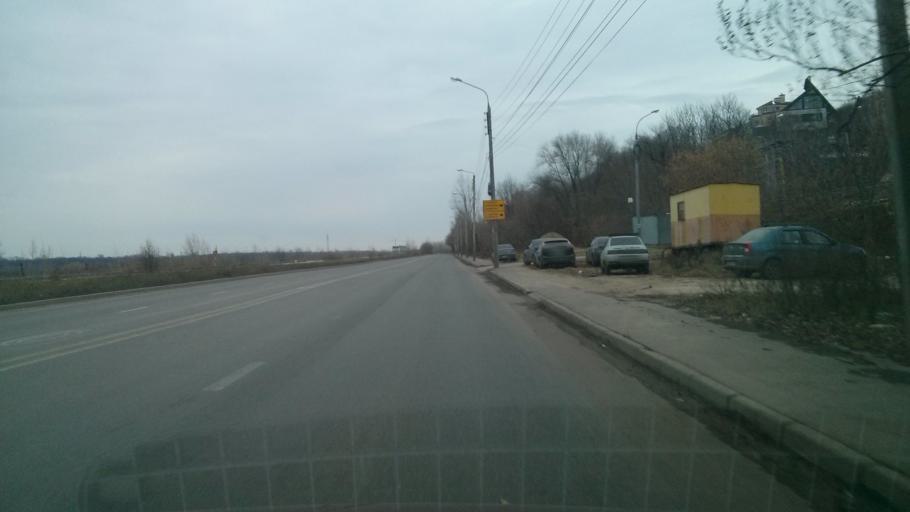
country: RU
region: Nizjnij Novgorod
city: Bor
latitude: 56.3169
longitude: 44.0803
